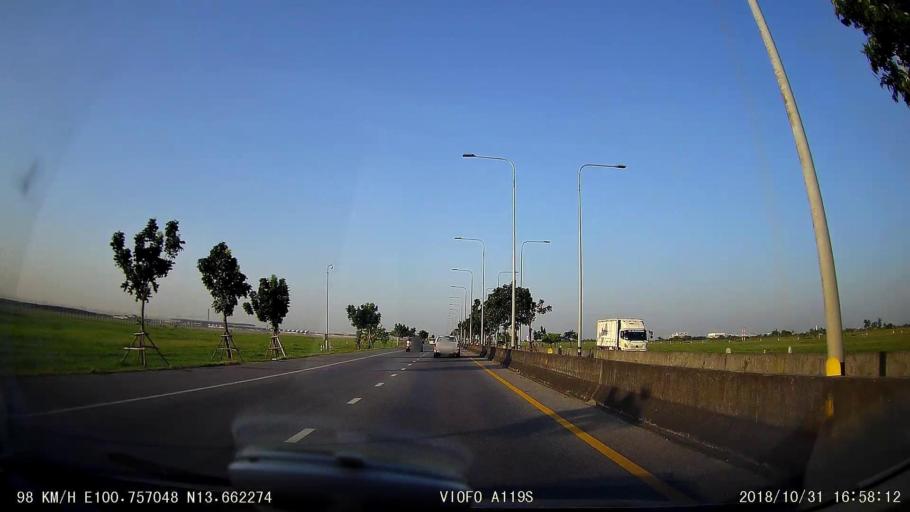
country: TH
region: Bangkok
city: Lat Krabang
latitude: 13.6626
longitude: 100.7571
